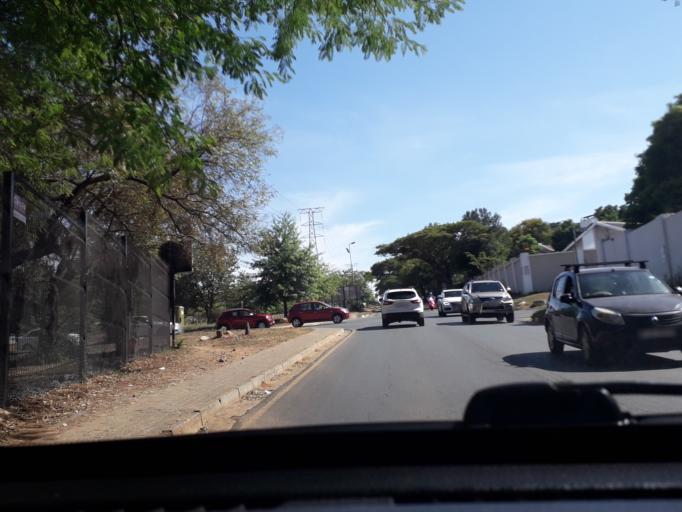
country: ZA
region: Gauteng
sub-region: City of Johannesburg Metropolitan Municipality
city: Johannesburg
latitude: -26.0991
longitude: 28.0380
